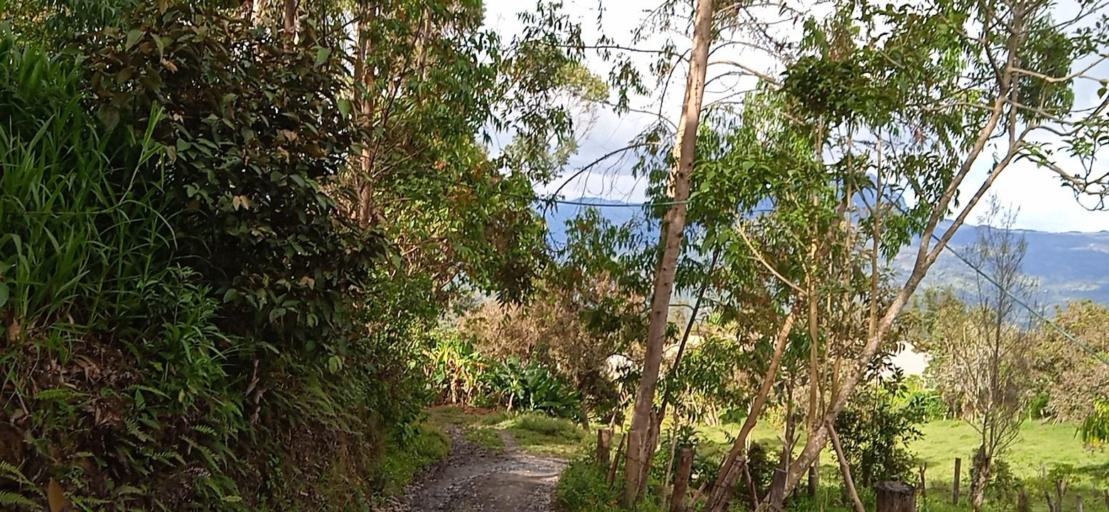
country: CO
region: Cundinamarca
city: Tenza
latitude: 5.0959
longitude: -73.4113
